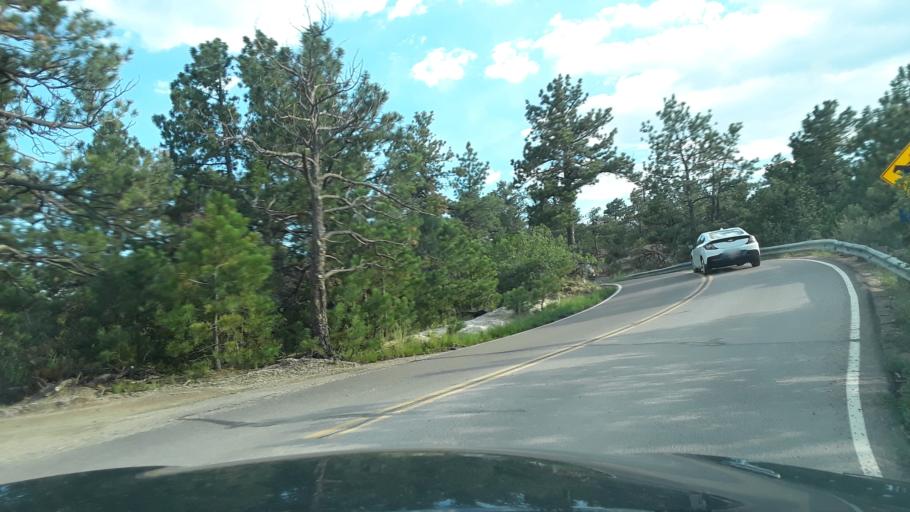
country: US
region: Colorado
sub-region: El Paso County
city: Colorado Springs
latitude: 38.8789
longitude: -104.7682
